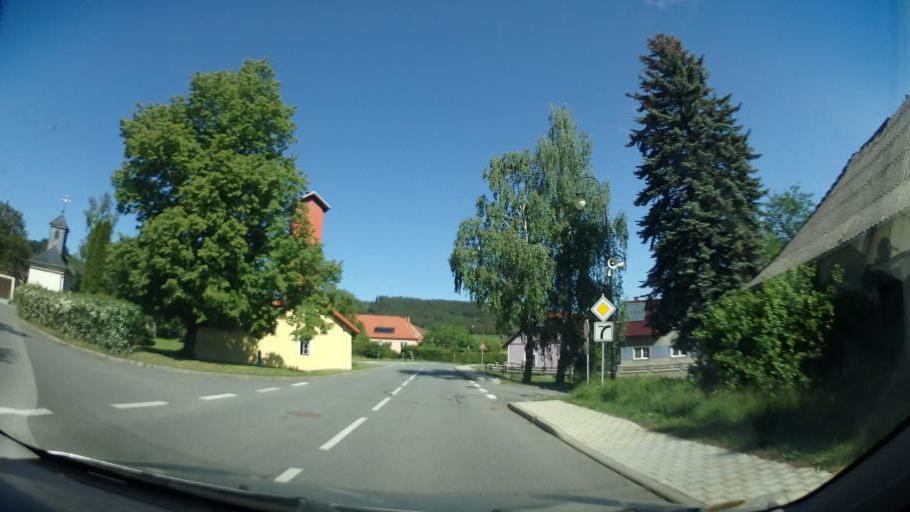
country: CZ
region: South Moravian
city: Velke Opatovice
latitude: 49.6291
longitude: 16.6085
